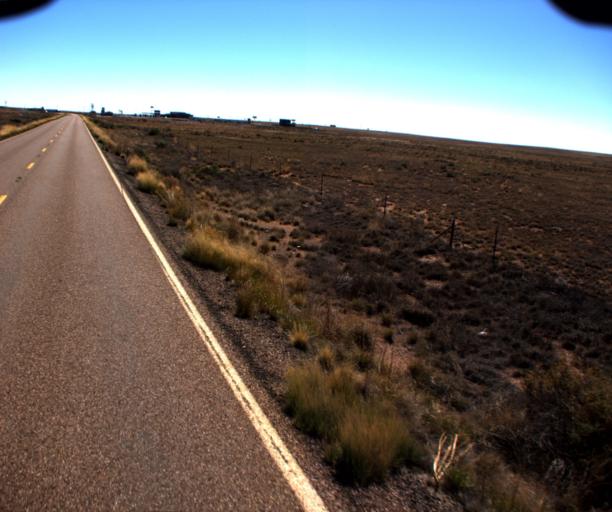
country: US
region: Arizona
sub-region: Navajo County
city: Holbrook
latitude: 34.9836
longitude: -110.0888
